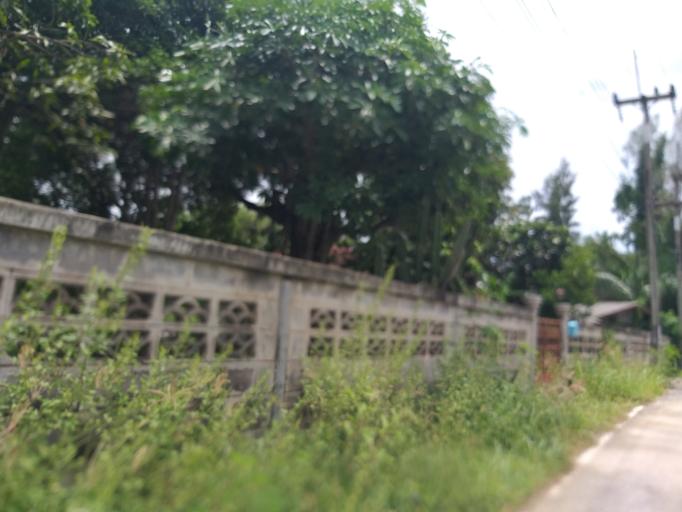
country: TH
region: Pathum Thani
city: Ban Lam Luk Ka
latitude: 13.9897
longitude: 100.8539
